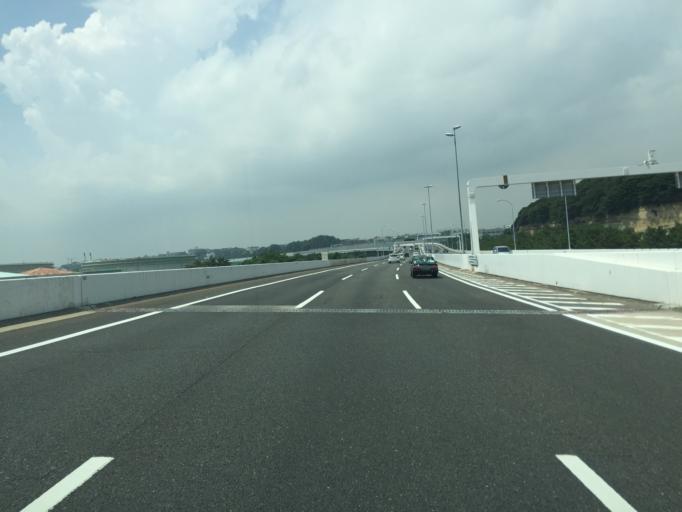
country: JP
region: Kanagawa
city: Yokohama
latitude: 35.4133
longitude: 139.6582
